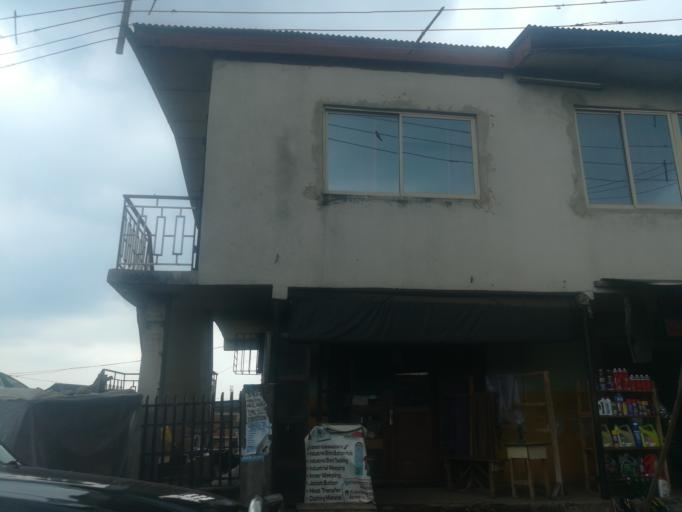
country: NG
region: Lagos
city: Ojota
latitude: 6.5966
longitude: 3.3866
